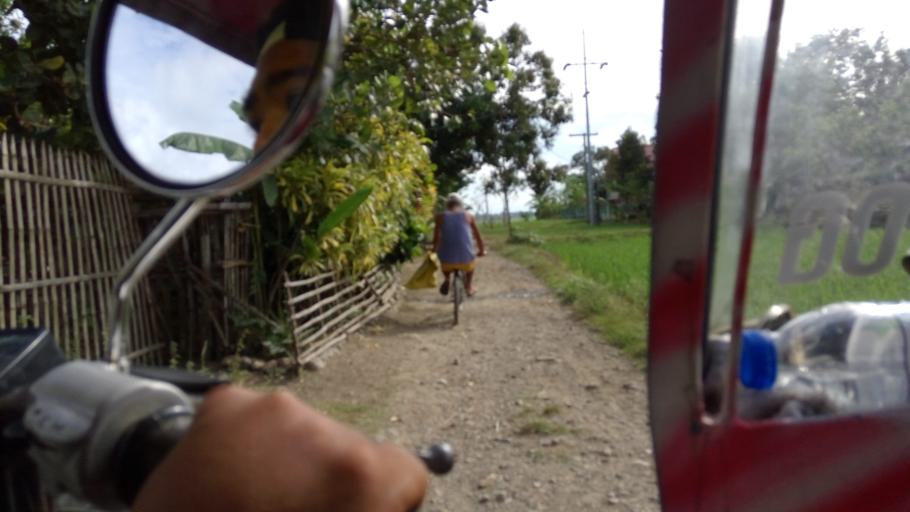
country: PH
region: Ilocos
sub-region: Province of La Union
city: San Eugenio
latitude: 16.3532
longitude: 120.3527
